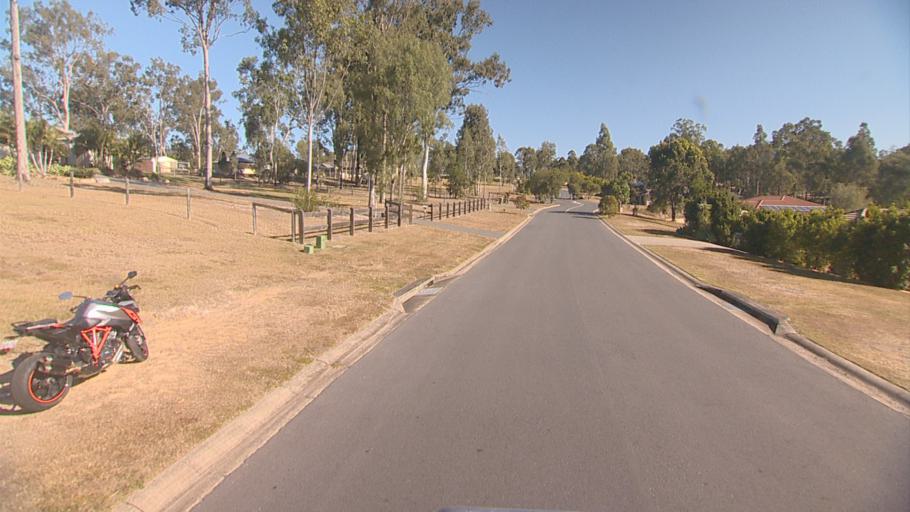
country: AU
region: Queensland
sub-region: Logan
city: Cedar Vale
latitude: -27.8638
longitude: 153.0374
